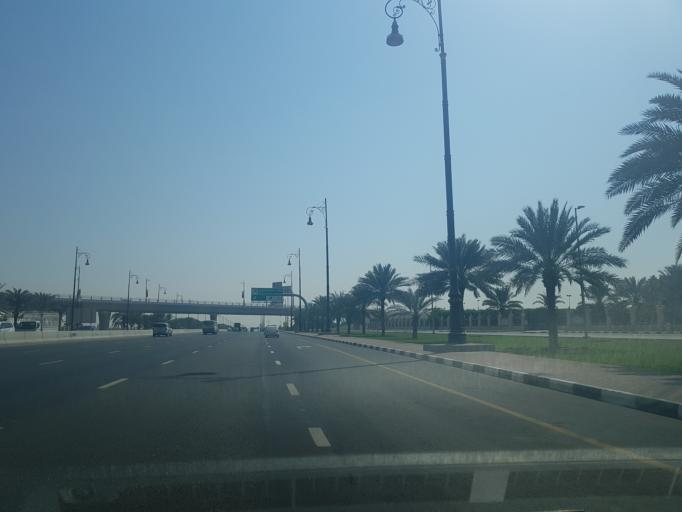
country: AE
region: Ash Shariqah
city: Sharjah
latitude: 25.3169
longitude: 55.5227
